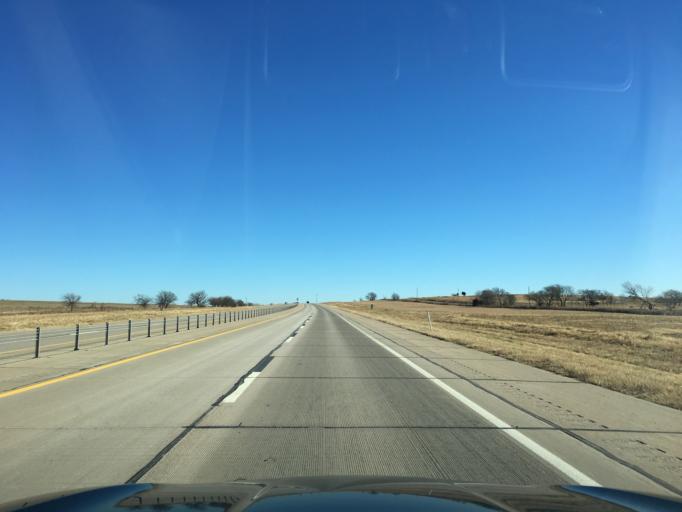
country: US
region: Oklahoma
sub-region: Noble County
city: Perry
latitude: 36.3923
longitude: -97.1873
